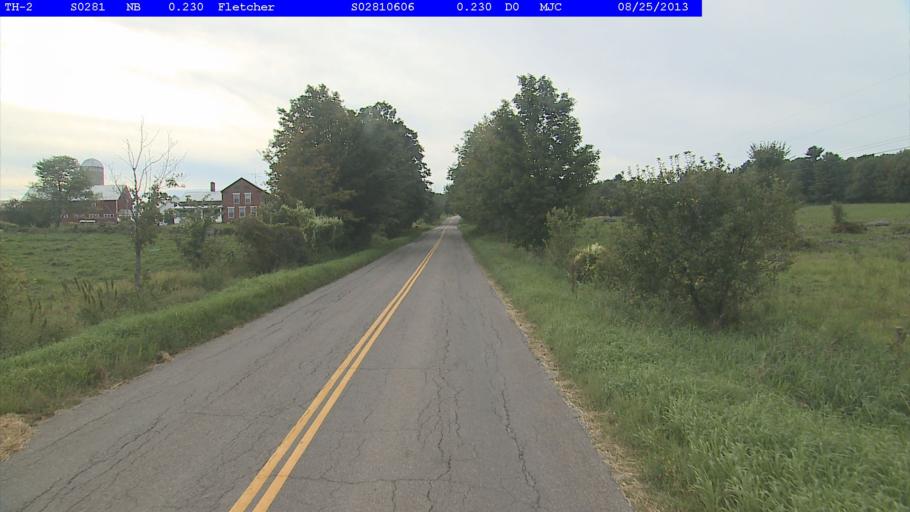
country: US
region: Vermont
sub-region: Chittenden County
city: Milton
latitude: 44.6848
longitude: -72.9184
